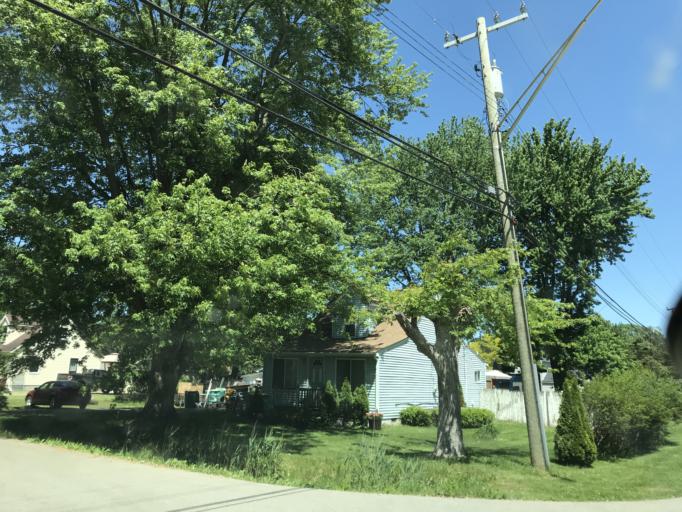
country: US
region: Michigan
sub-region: Wayne County
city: Woodhaven
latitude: 42.1740
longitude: -83.2999
